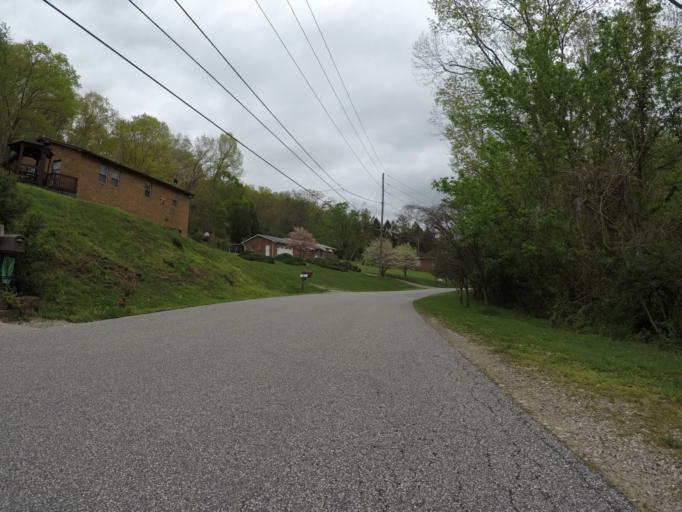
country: US
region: West Virginia
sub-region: Cabell County
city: Barboursville
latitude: 38.4077
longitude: -82.2849
